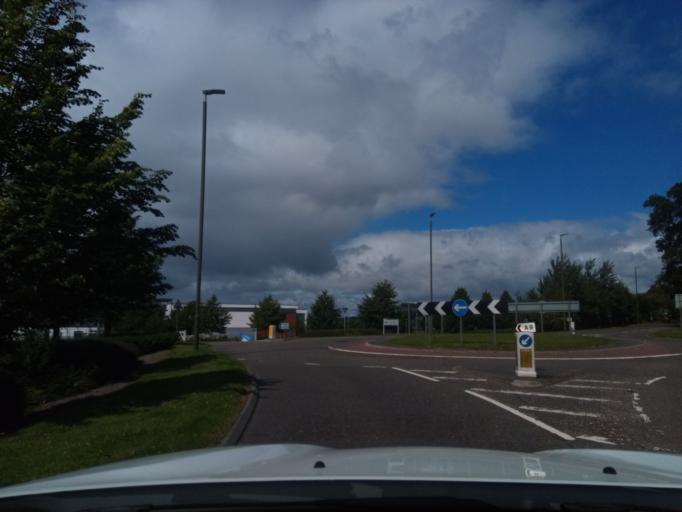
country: GB
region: Scotland
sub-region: Stirling
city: Stirling
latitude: 56.1401
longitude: -3.9257
